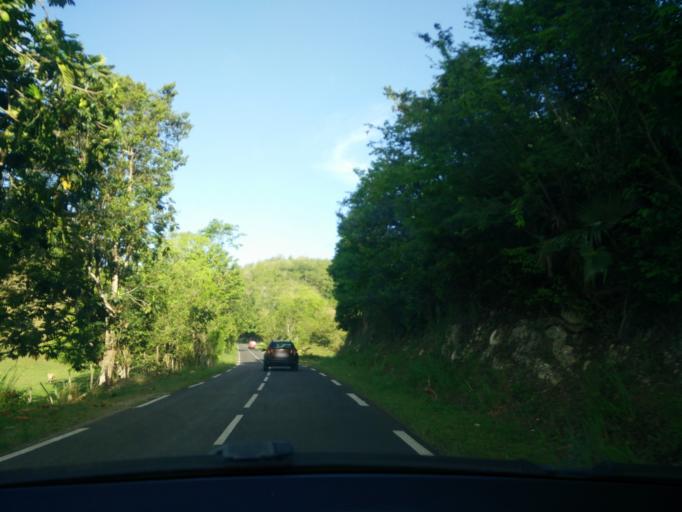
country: GP
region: Guadeloupe
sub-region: Guadeloupe
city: Sainte-Anne
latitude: 16.2773
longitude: -61.4201
